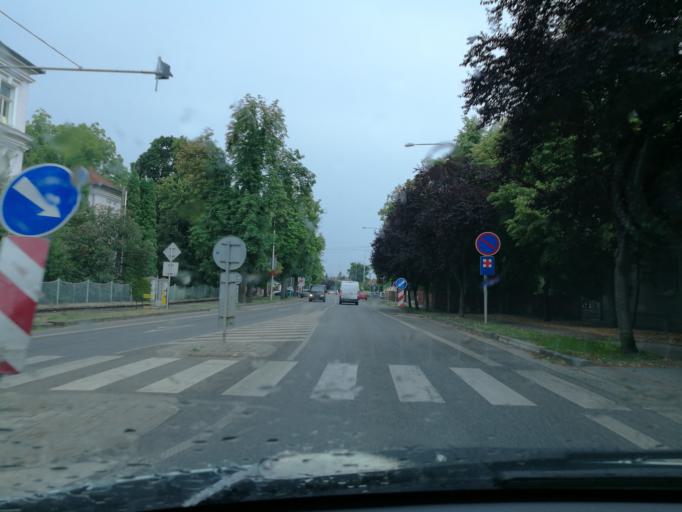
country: SK
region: Nitriansky
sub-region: Okres Komarno
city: Hurbanovo
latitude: 47.8731
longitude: 18.1915
